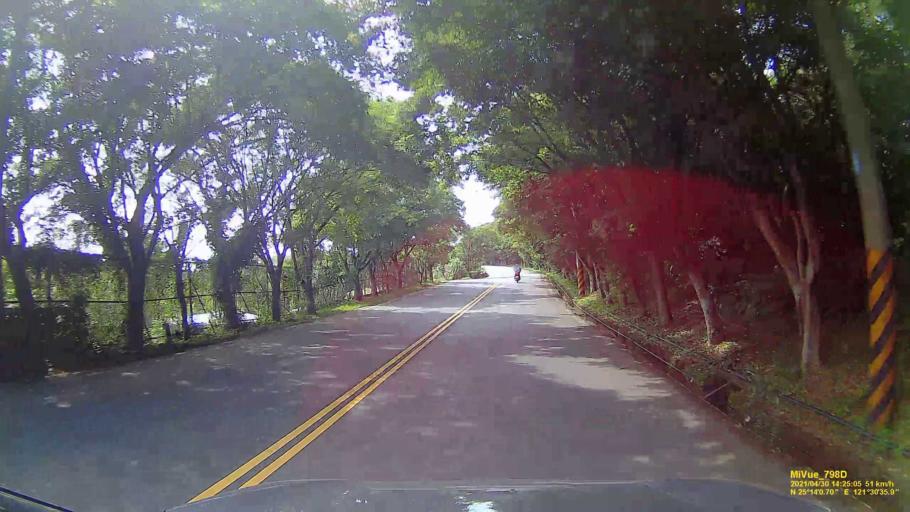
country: TW
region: Taipei
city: Taipei
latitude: 25.2338
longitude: 121.5098
